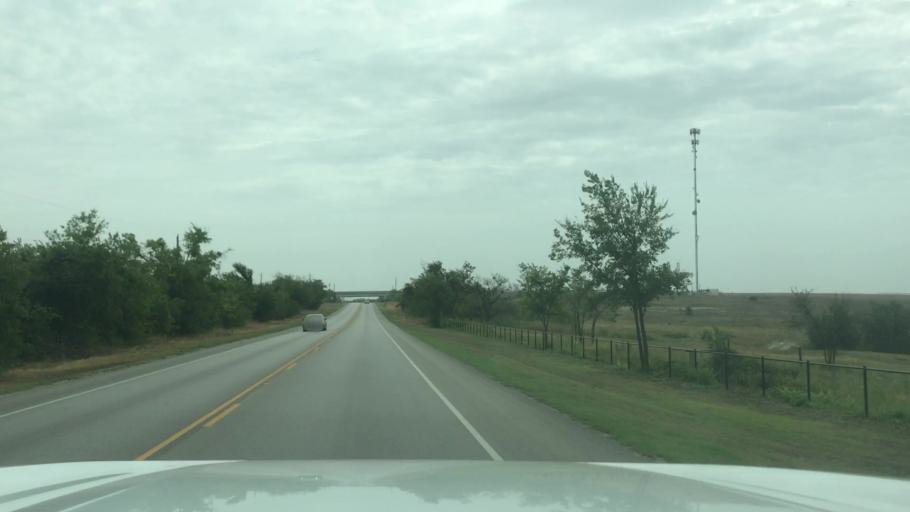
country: US
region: Texas
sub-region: Erath County
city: Dublin
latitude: 32.0949
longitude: -98.3738
